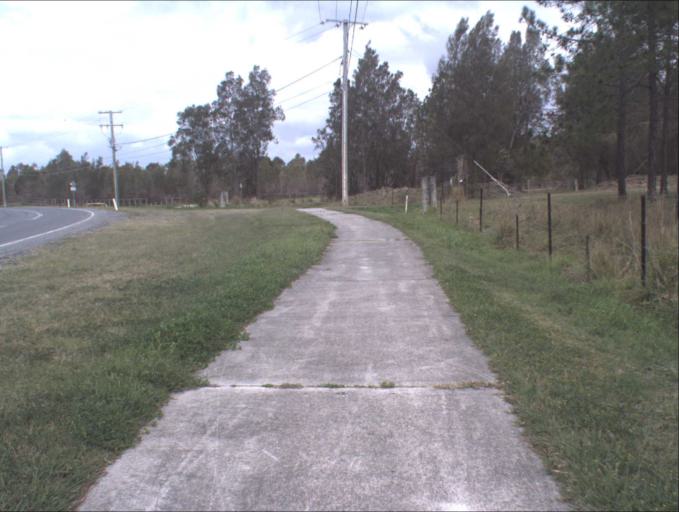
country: AU
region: Queensland
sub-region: Logan
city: Waterford West
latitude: -27.6964
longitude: 153.1180
